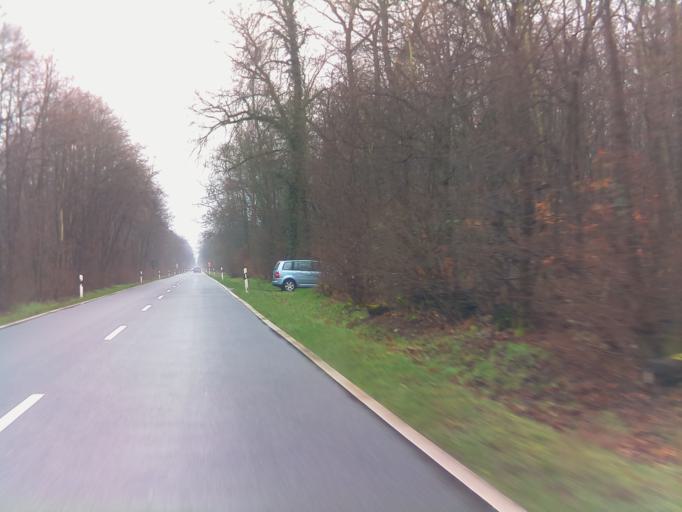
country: DE
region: Hesse
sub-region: Regierungsbezirk Darmstadt
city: Gross-Rohrheim
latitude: 49.7016
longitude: 8.5155
